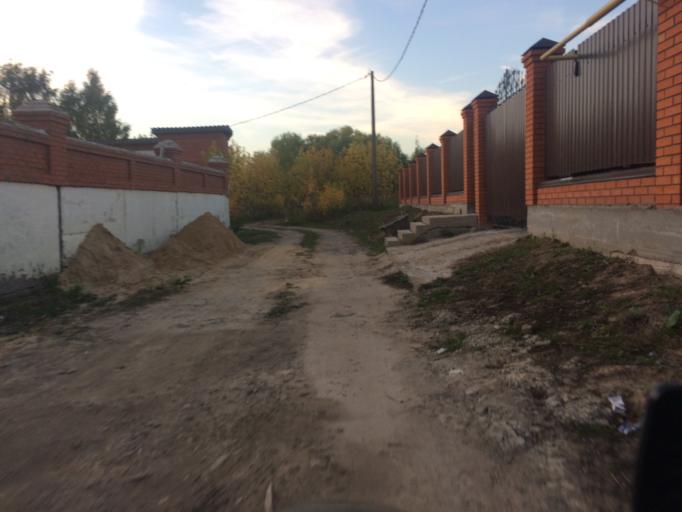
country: RU
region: Mariy-El
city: Yoshkar-Ola
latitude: 56.6443
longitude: 47.9160
